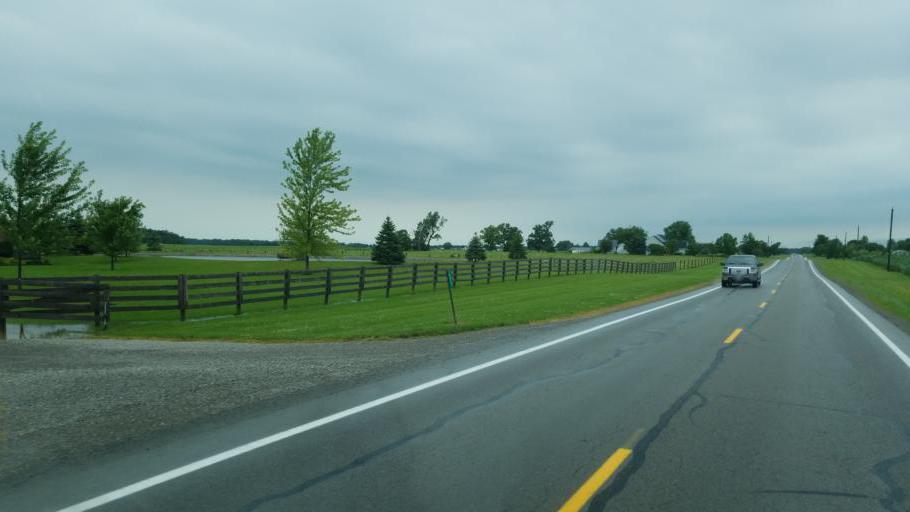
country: US
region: Ohio
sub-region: Hardin County
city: Kenton
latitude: 40.6019
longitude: -83.5945
